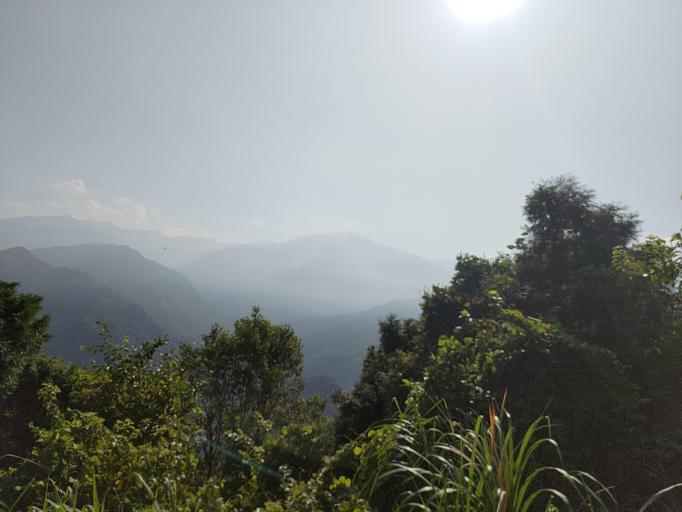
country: TW
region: Taiwan
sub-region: Hsinchu
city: Hsinchu
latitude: 24.6039
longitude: 121.0935
